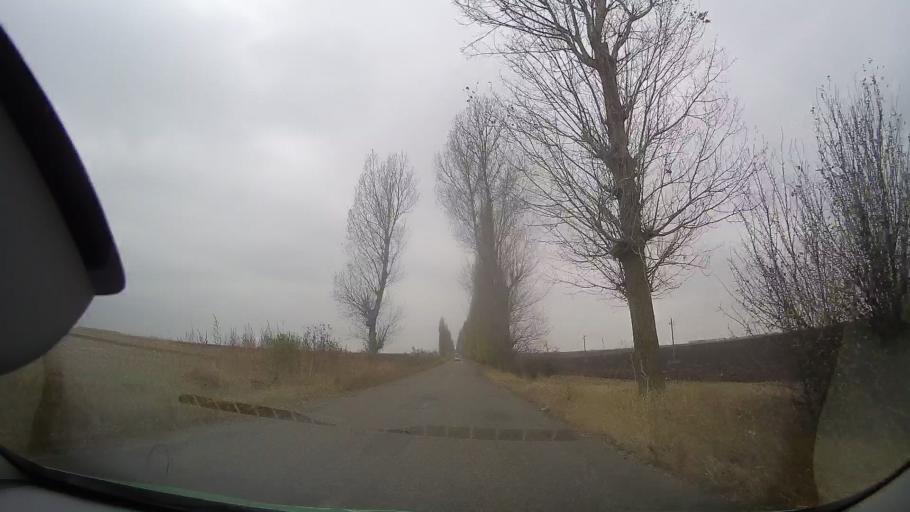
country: RO
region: Buzau
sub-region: Comuna Scutelnici
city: Scutelnici
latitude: 44.8452
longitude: 26.8813
